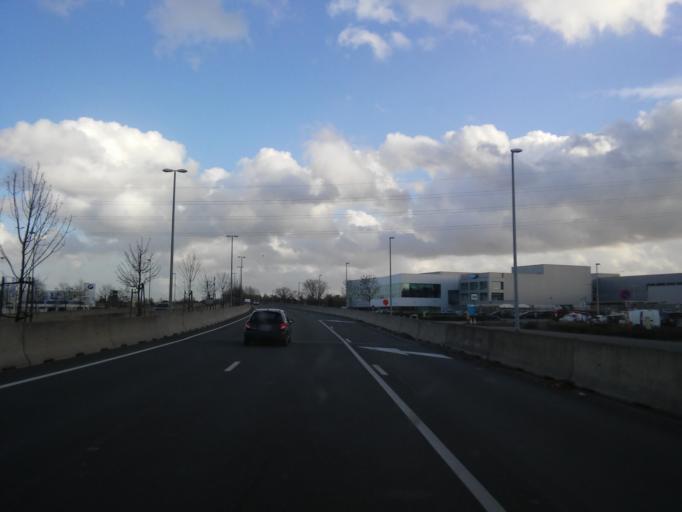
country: BE
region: Flanders
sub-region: Provincie Antwerpen
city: Puurs
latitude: 51.0623
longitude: 4.3220
